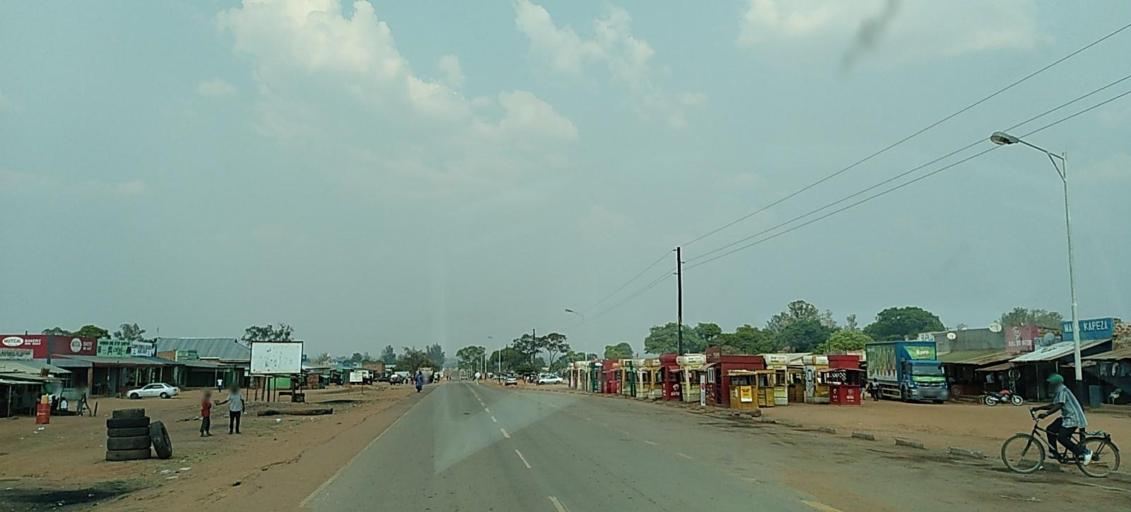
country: ZM
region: North-Western
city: Kabompo
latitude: -13.5939
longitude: 24.1997
